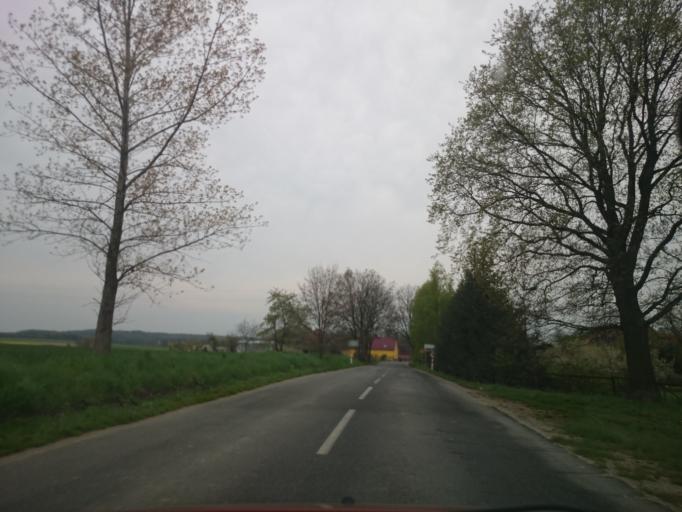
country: PL
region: Lower Silesian Voivodeship
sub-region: Powiat strzelinski
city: Przeworno
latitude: 50.6464
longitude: 17.2290
